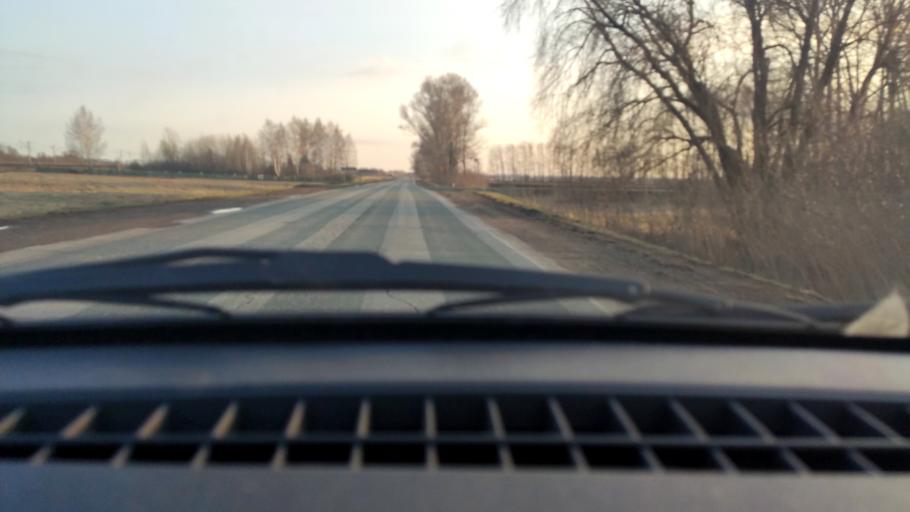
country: RU
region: Bashkortostan
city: Chishmy
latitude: 54.4505
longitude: 55.2476
